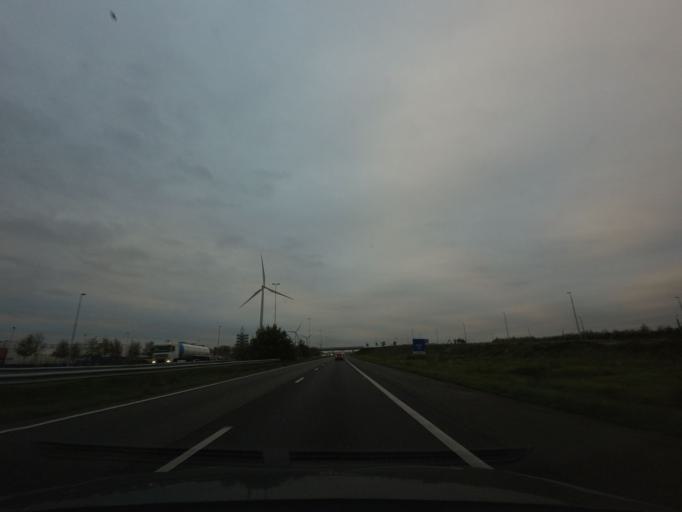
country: NL
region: North Brabant
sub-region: Gemeente Zundert
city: Zundert
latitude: 51.4949
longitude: 4.7401
